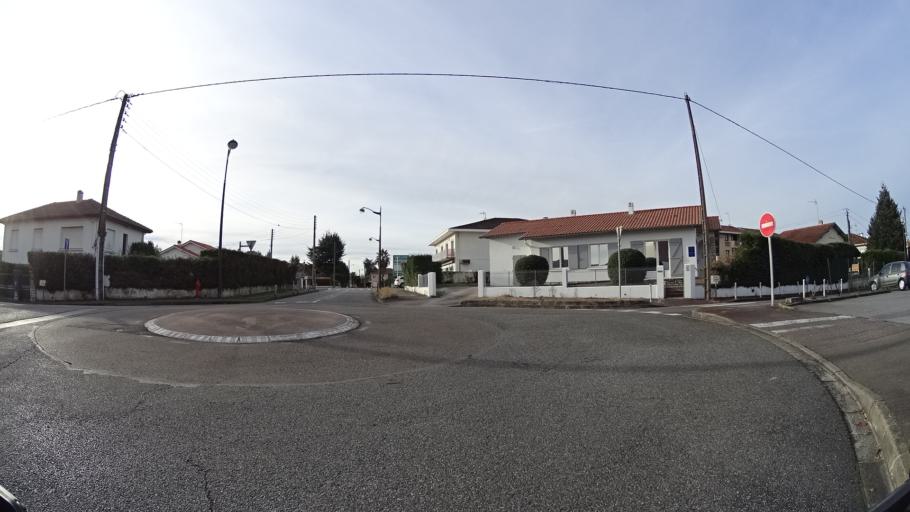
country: FR
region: Aquitaine
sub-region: Departement des Landes
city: Saint-Paul-les-Dax
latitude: 43.7292
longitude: -1.0498
